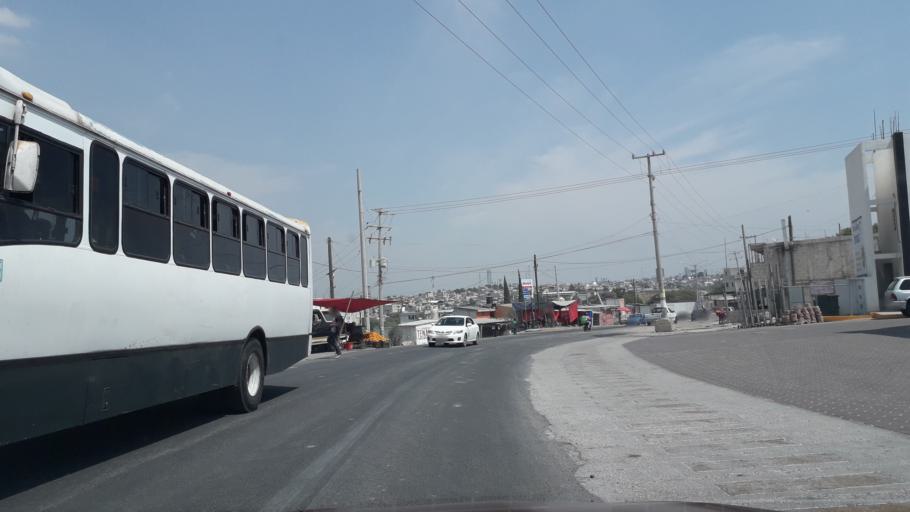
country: MX
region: Puebla
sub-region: Puebla
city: El Capulo (La Quebradora)
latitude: 18.9478
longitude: -98.2693
